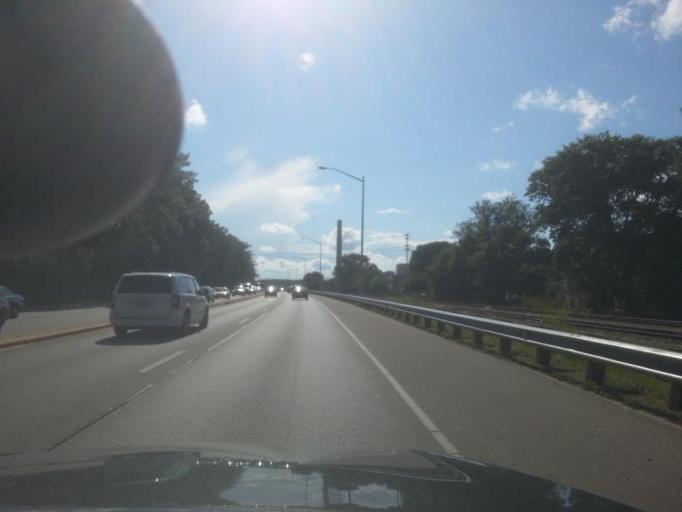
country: US
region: Wisconsin
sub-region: Dane County
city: Madison
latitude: 43.0742
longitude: -89.4173
